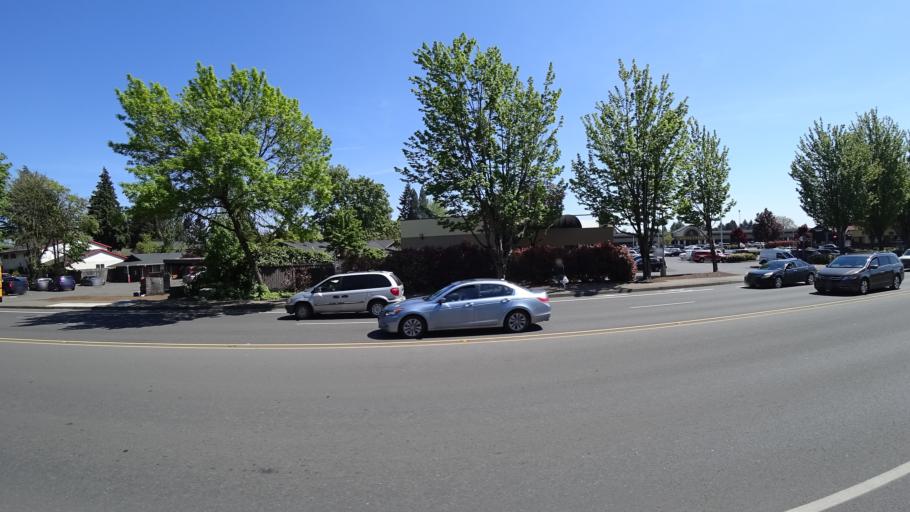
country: US
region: Oregon
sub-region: Washington County
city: Hillsboro
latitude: 45.5127
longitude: -122.9739
